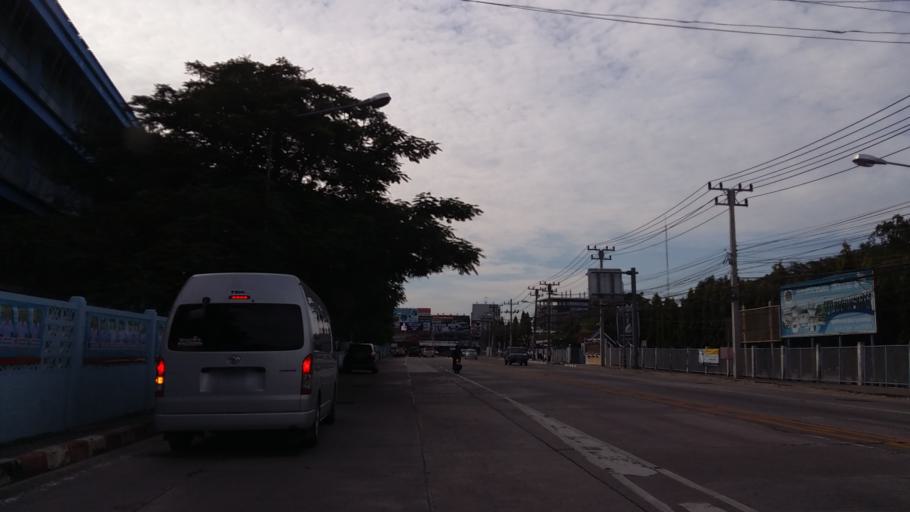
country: TH
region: Chon Buri
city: Chon Buri
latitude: 13.3507
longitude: 100.9775
